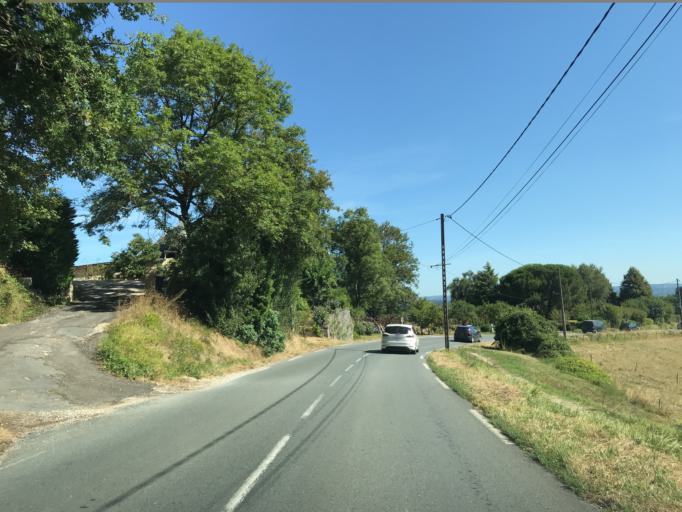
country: FR
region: Limousin
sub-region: Departement de la Correze
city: Larche
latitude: 45.1080
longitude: 1.3880
